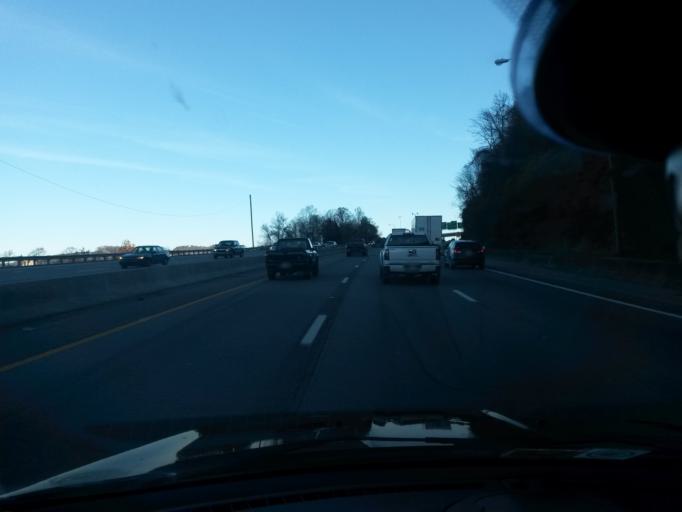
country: US
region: West Virginia
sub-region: Kanawha County
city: Charleston
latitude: 38.3568
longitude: -81.6565
